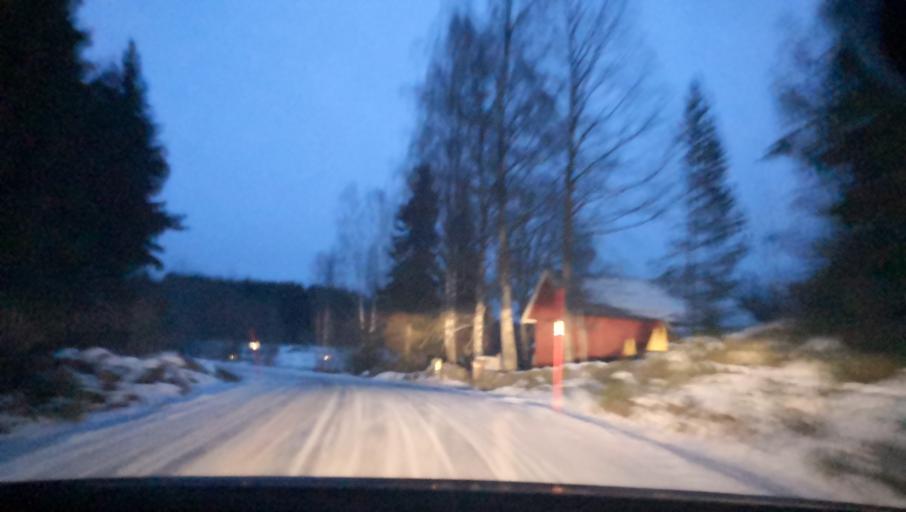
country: SE
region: Uppsala
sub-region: Heby Kommun
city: Tarnsjo
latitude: 60.2432
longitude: 16.7128
